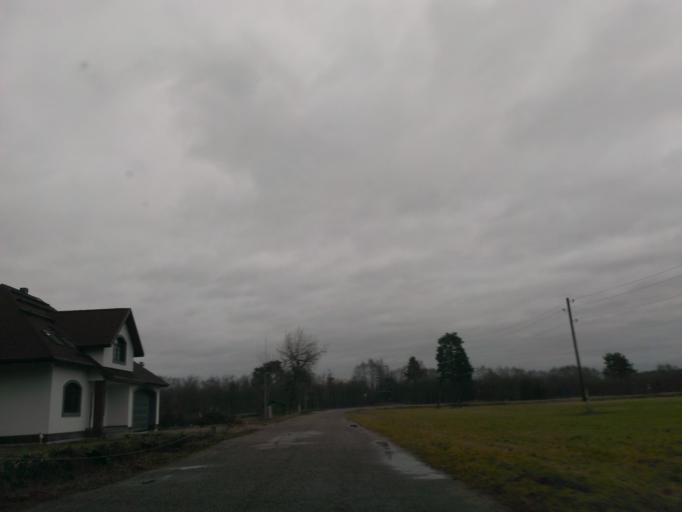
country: LV
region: Adazi
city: Adazi
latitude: 57.0636
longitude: 24.3570
